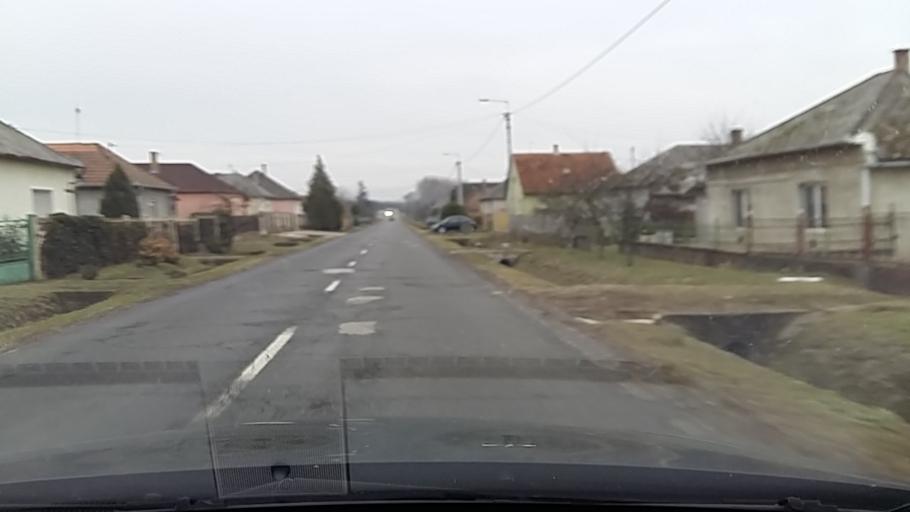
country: HU
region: Szabolcs-Szatmar-Bereg
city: Kek
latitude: 48.1014
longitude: 21.8825
